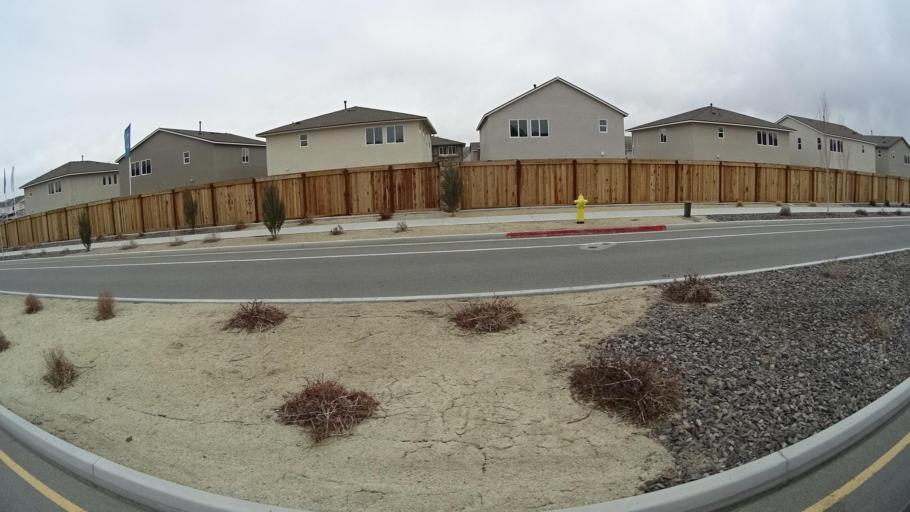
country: US
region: Nevada
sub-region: Washoe County
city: Spanish Springs
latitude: 39.6119
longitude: -119.7194
